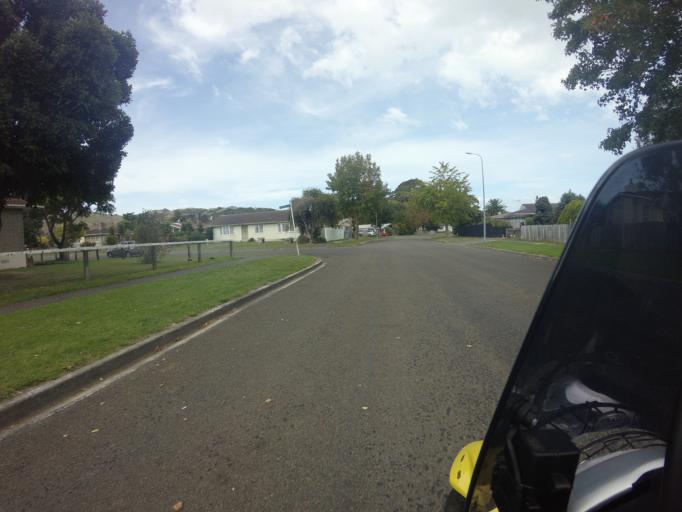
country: NZ
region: Gisborne
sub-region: Gisborne District
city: Gisborne
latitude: -38.6760
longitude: 178.0518
